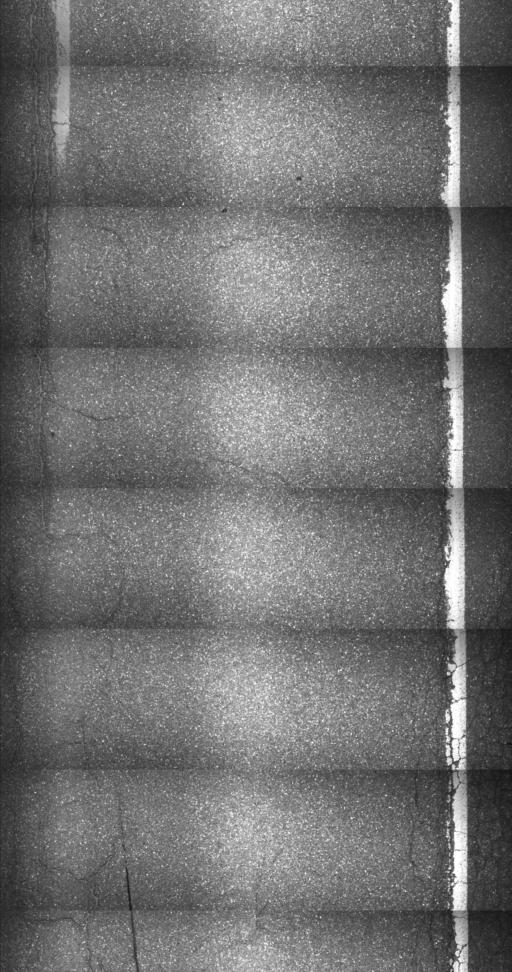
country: US
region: Vermont
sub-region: Addison County
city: Bristol
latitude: 44.1746
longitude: -73.0570
